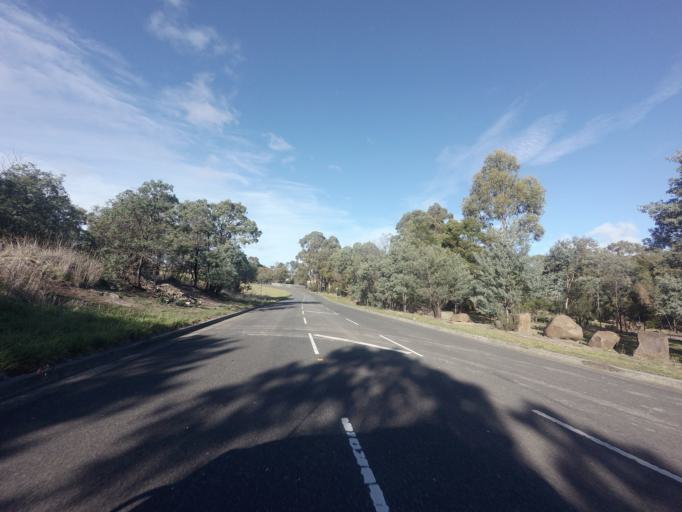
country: AU
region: Tasmania
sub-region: Clarence
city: Rokeby
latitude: -42.8879
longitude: 147.4378
